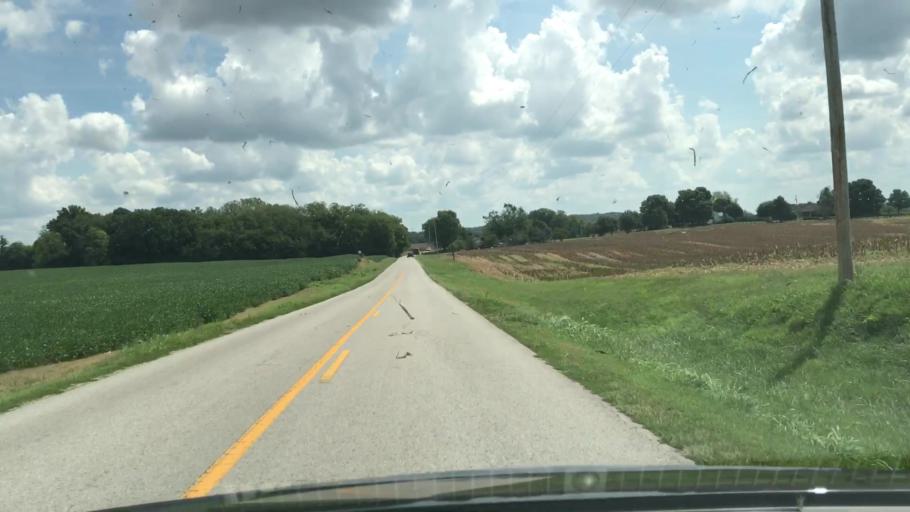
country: US
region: Kentucky
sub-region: Todd County
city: Guthrie
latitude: 36.7110
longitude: -87.0544
